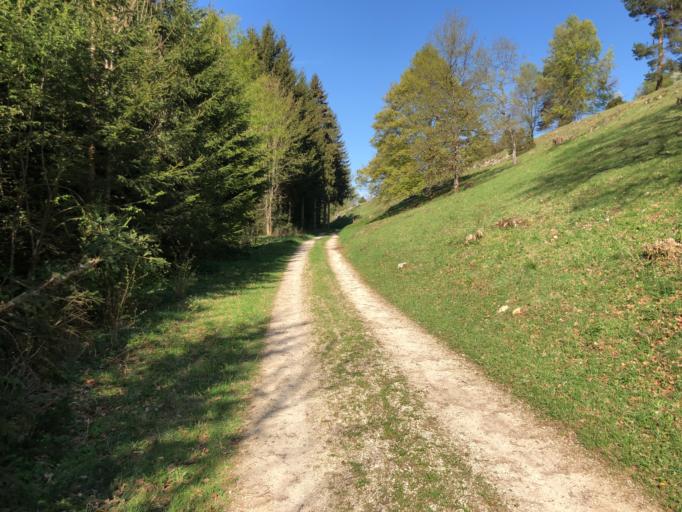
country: DE
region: Baden-Wuerttemberg
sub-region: Tuebingen Region
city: Berghulen
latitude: 48.4806
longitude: 9.7555
